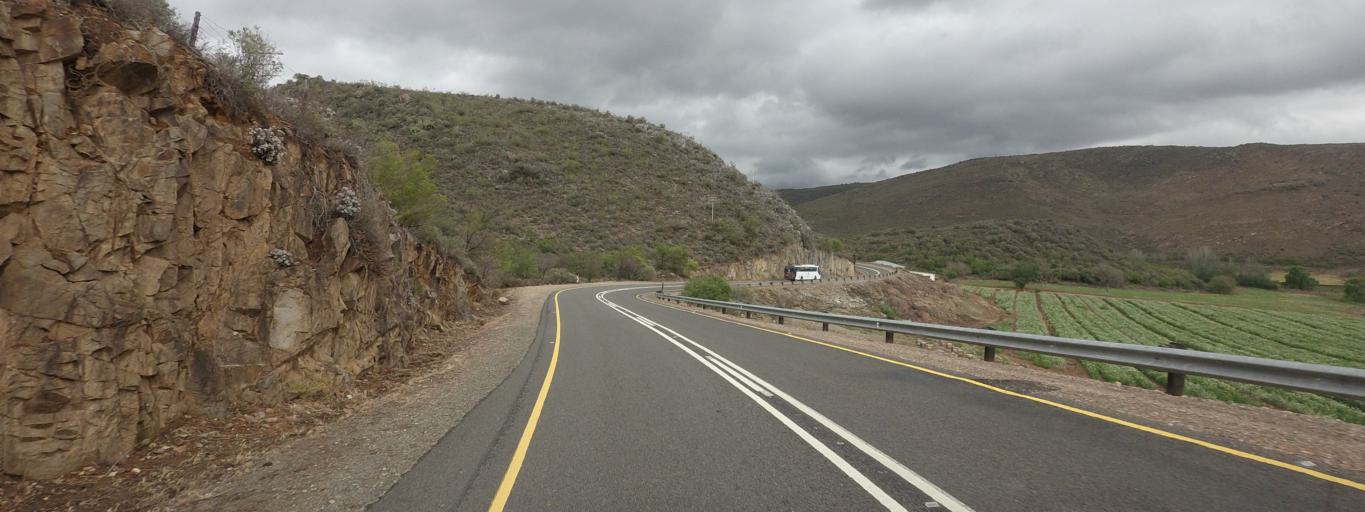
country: ZA
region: Western Cape
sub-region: Eden District Municipality
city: Oudtshoorn
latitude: -33.4145
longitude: 22.2362
